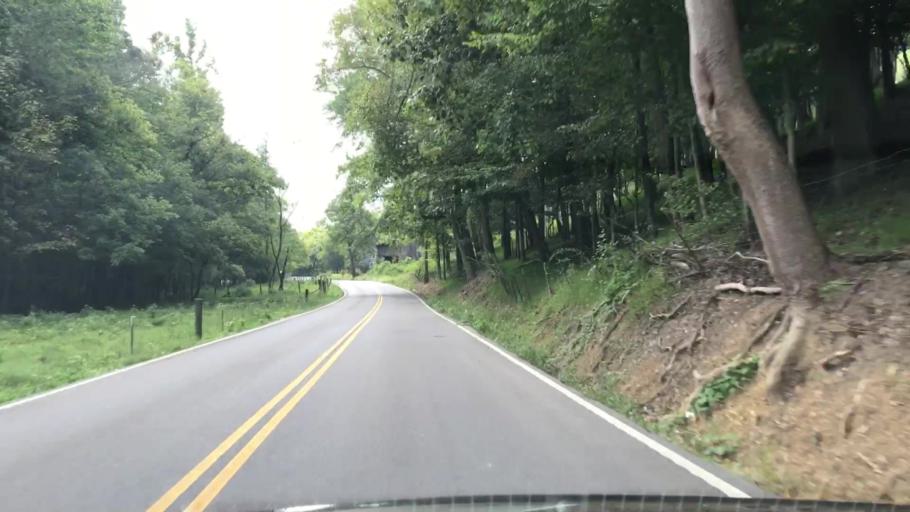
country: US
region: Tennessee
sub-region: Sumner County
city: Westmoreland
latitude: 36.4903
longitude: -86.1914
